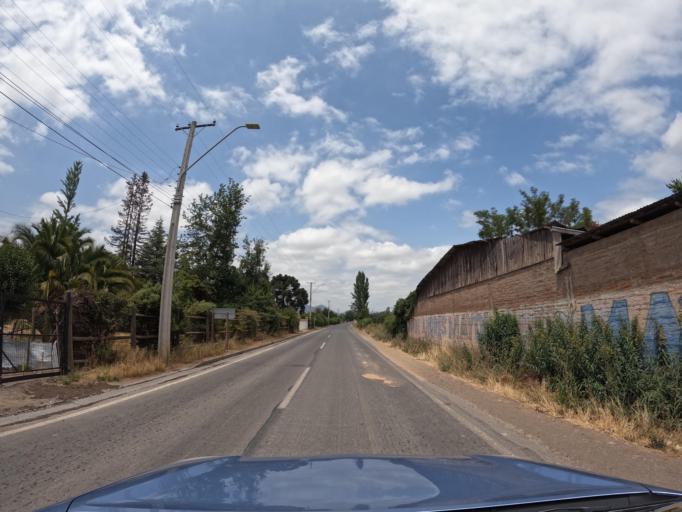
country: CL
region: O'Higgins
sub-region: Provincia de Colchagua
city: Chimbarongo
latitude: -34.7539
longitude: -70.9537
